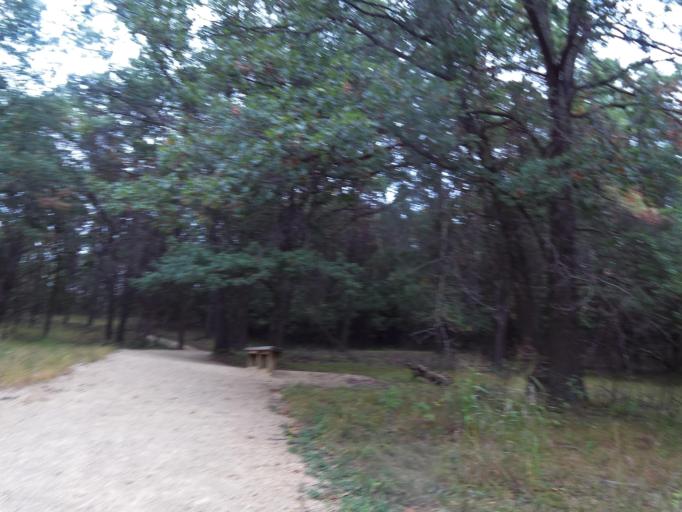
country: US
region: Minnesota
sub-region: Washington County
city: Afton
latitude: 44.8616
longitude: -92.7755
